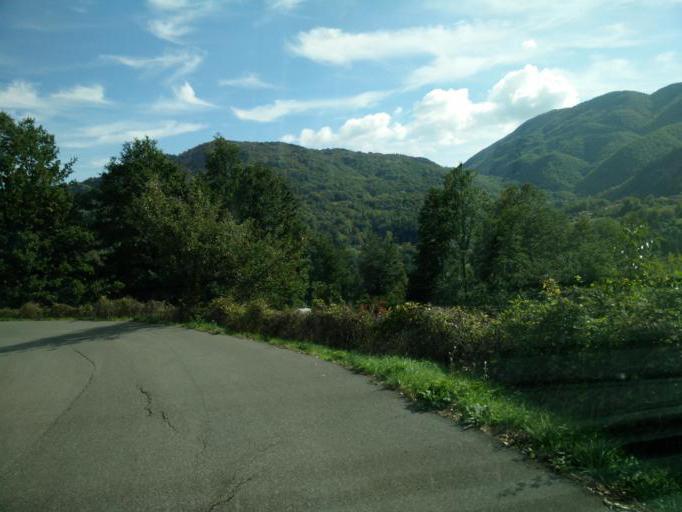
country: IT
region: Tuscany
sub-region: Provincia di Massa-Carrara
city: Patigno
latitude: 44.3492
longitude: 9.7635
